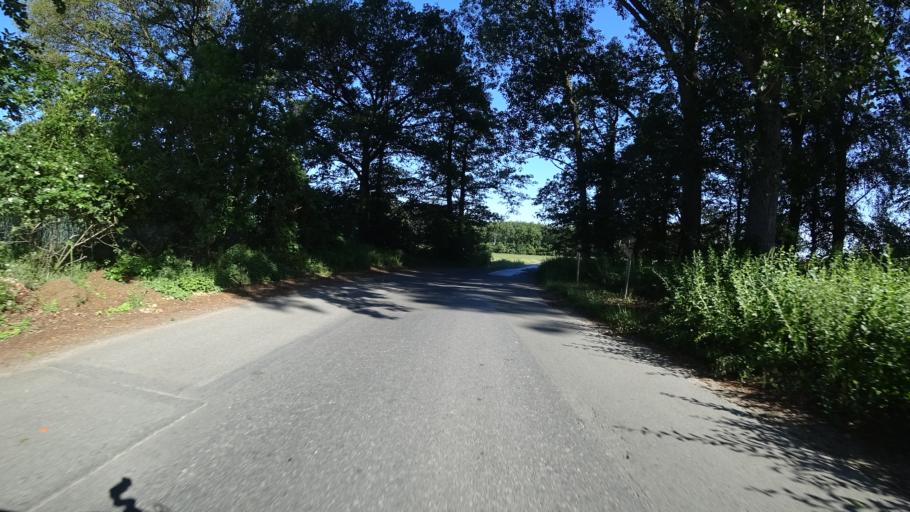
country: DE
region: North Rhine-Westphalia
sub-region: Regierungsbezirk Detmold
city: Guetersloh
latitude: 51.9151
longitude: 8.3256
